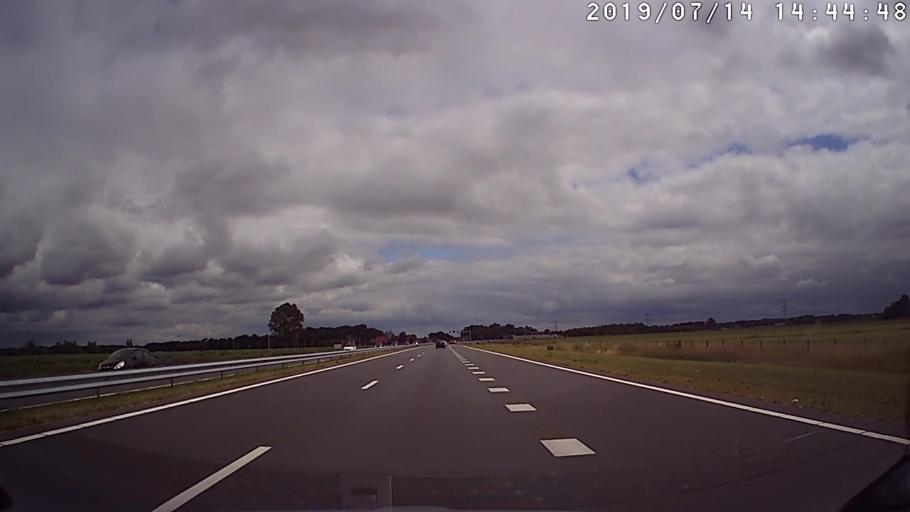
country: NL
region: Overijssel
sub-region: Gemeente Raalte
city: Heino
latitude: 52.4816
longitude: 6.1822
